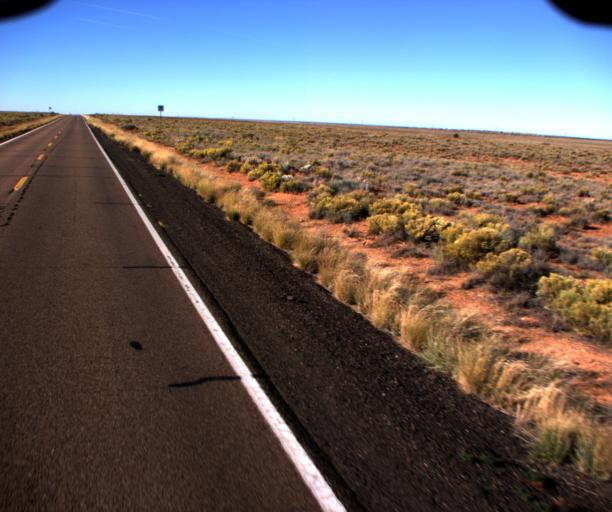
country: US
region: Arizona
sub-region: Navajo County
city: Holbrook
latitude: 34.8339
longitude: -110.1860
